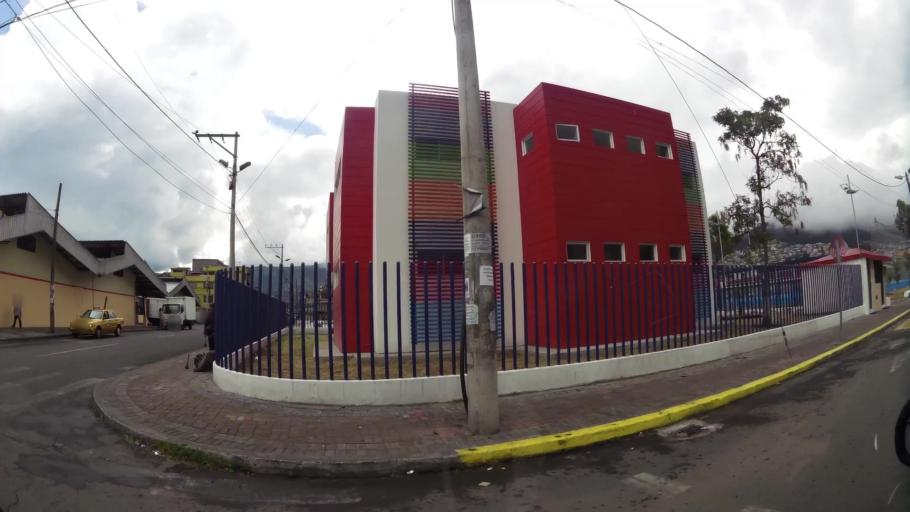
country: EC
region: Pichincha
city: Quito
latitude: -0.2684
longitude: -78.5428
